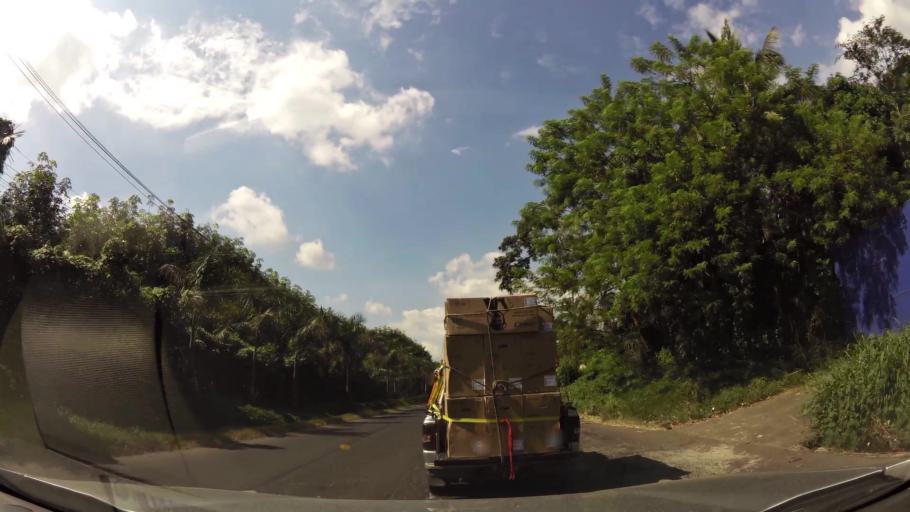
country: GT
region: Suchitepeque
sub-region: Municipio de Cuyotenango
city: Cuyotenango
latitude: 14.5422
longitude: -91.5440
